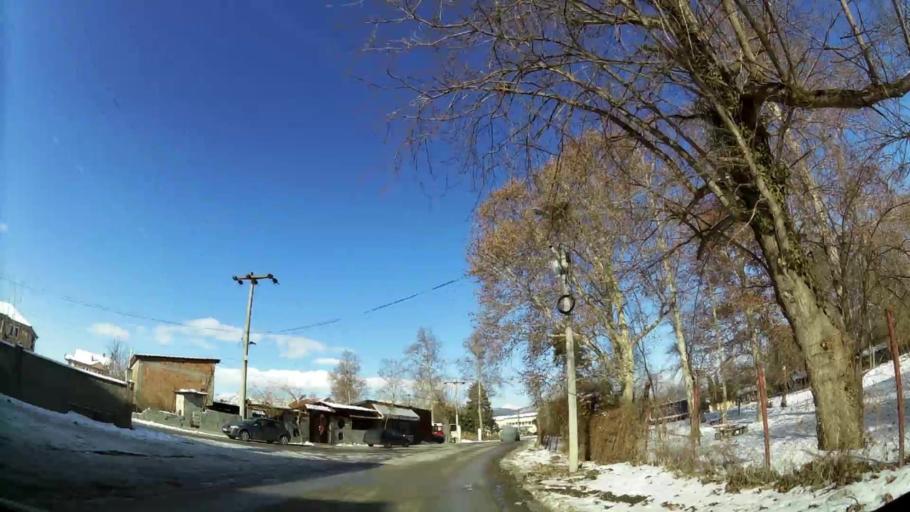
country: MK
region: Saraj
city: Saraj
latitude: 42.0006
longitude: 21.3374
